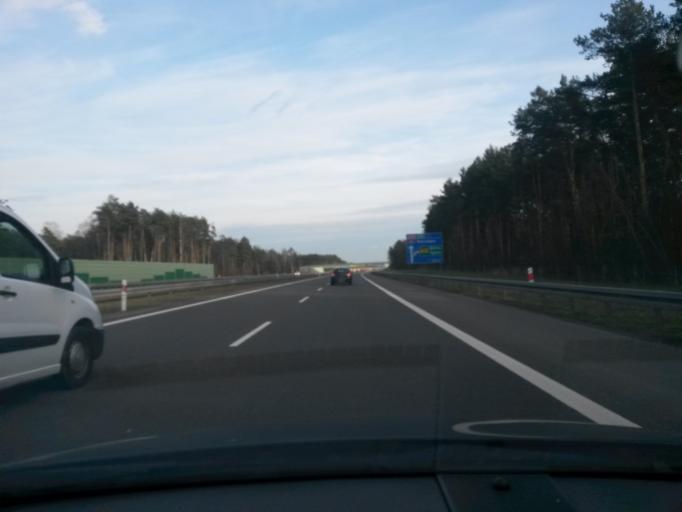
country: PL
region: Lodz Voivodeship
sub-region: Powiat zgierski
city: Zgierz
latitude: 51.9142
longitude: 19.4275
